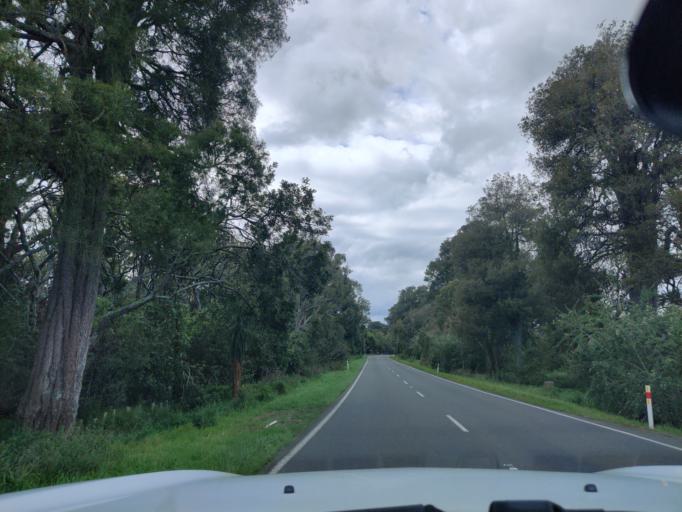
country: NZ
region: Manawatu-Wanganui
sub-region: Palmerston North City
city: Palmerston North
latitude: -40.2475
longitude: 175.5373
